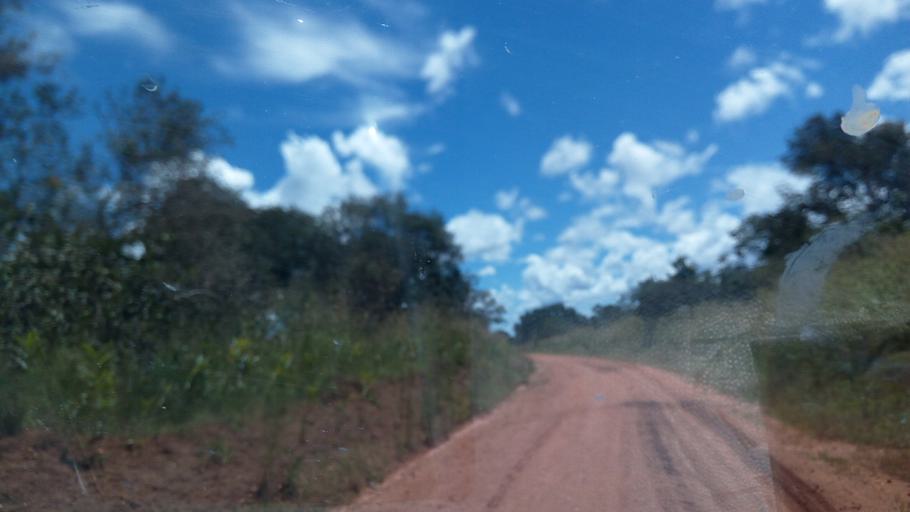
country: CD
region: Katanga
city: Kalemie
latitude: -5.4244
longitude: 28.9365
